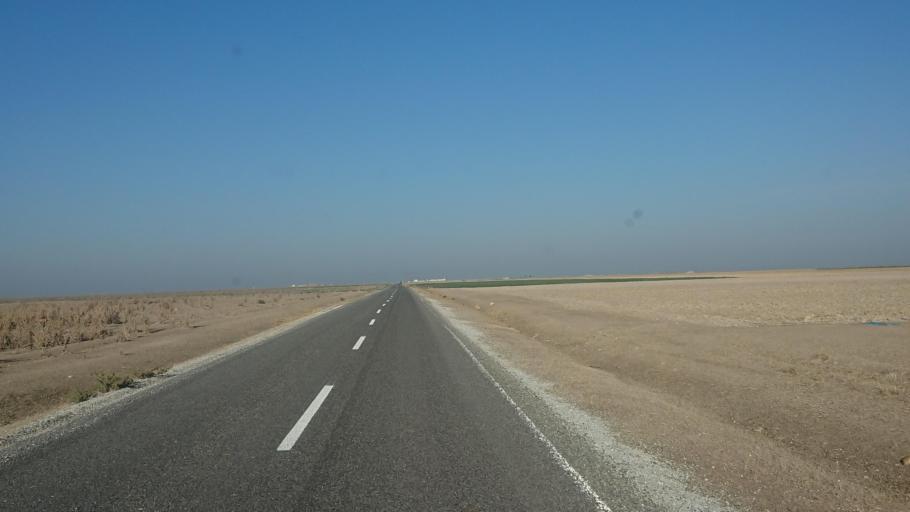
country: TR
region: Aksaray
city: Yesilova
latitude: 38.3878
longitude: 33.7702
